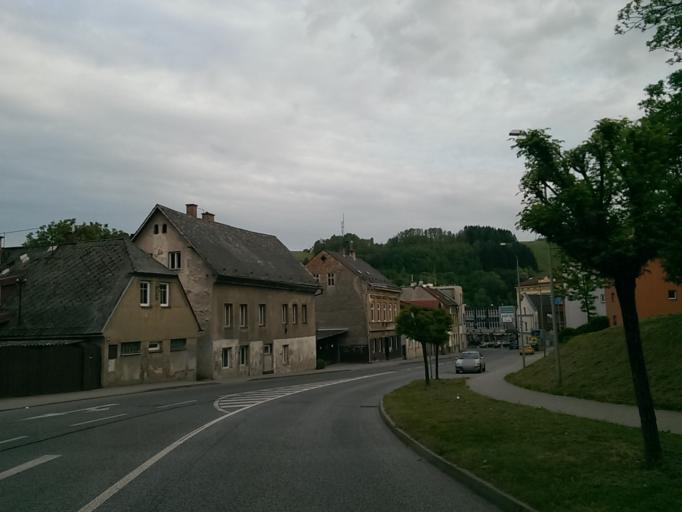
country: CZ
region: Liberecky
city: Zelezny Brod
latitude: 50.6441
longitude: 15.2538
